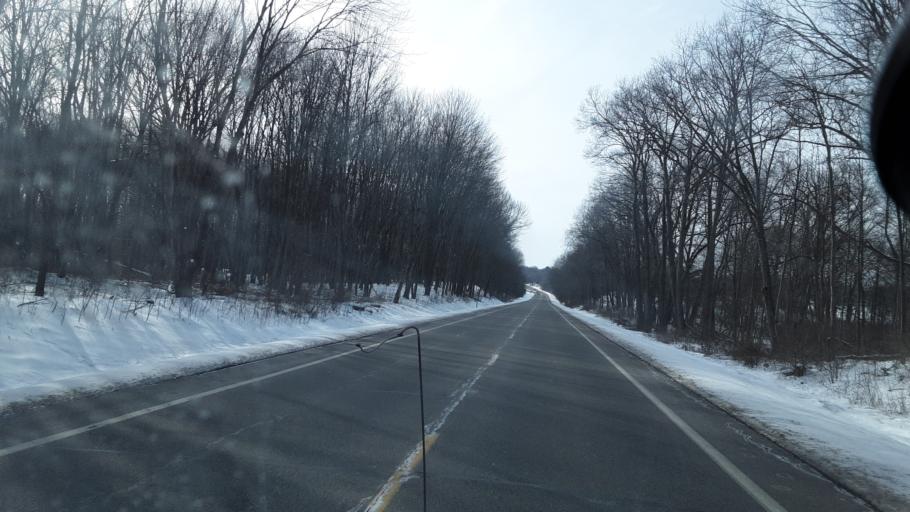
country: US
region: Ohio
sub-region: Stark County
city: Hartville
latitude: 41.0270
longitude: -81.3363
